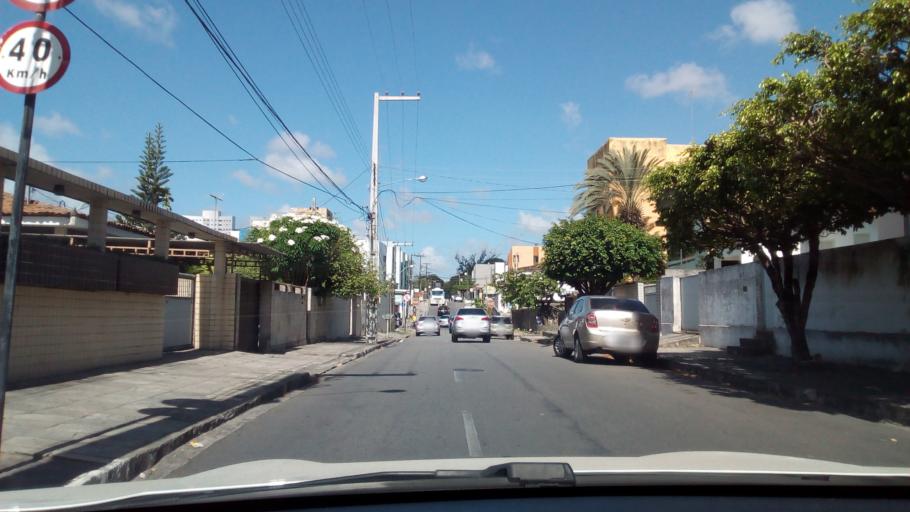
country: BR
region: Paraiba
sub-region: Joao Pessoa
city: Joao Pessoa
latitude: -7.1496
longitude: -34.8457
